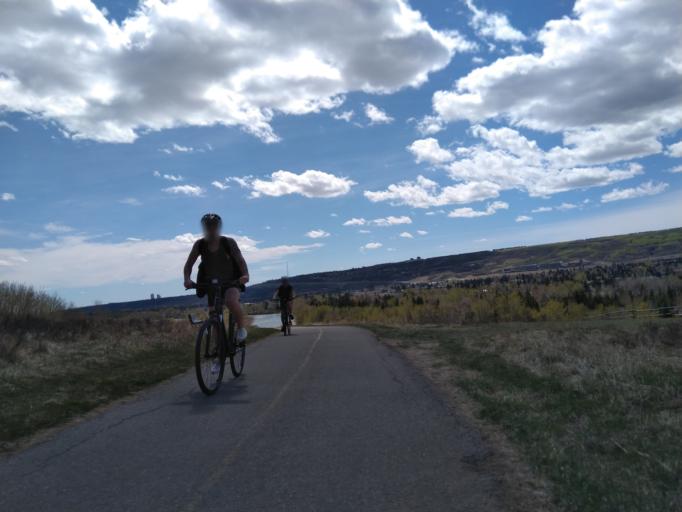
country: CA
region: Alberta
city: Calgary
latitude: 51.0987
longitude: -114.1903
